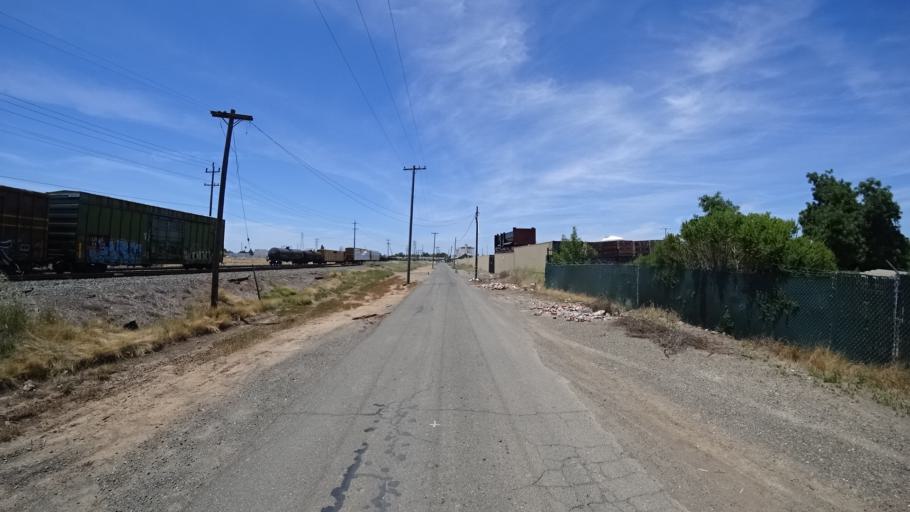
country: US
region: California
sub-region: Sacramento County
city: Florin
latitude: 38.5324
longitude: -121.4042
